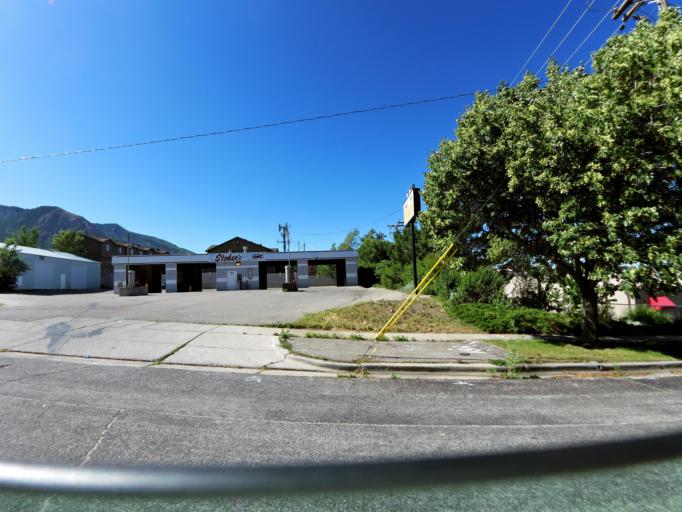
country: US
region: Utah
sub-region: Weber County
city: Ogden
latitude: 41.2308
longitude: -111.9461
